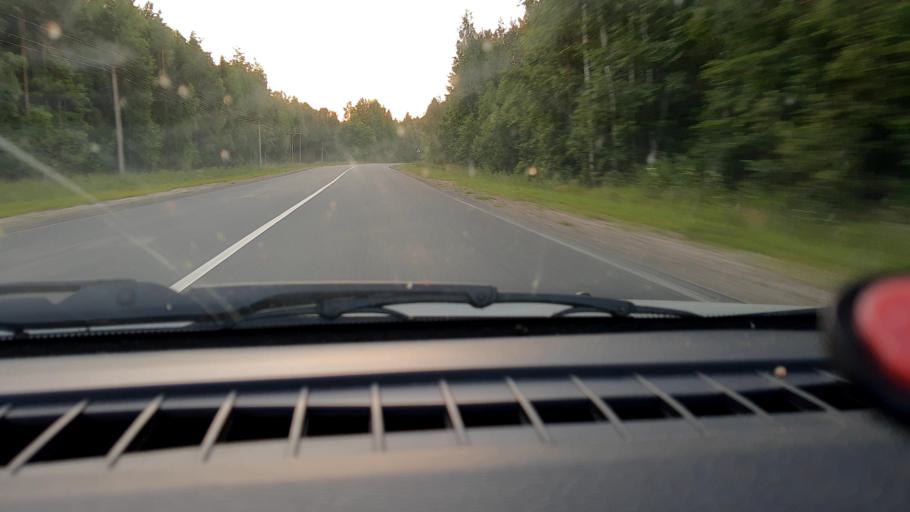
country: RU
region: Nizjnij Novgorod
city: Uren'
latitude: 57.3843
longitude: 45.6874
